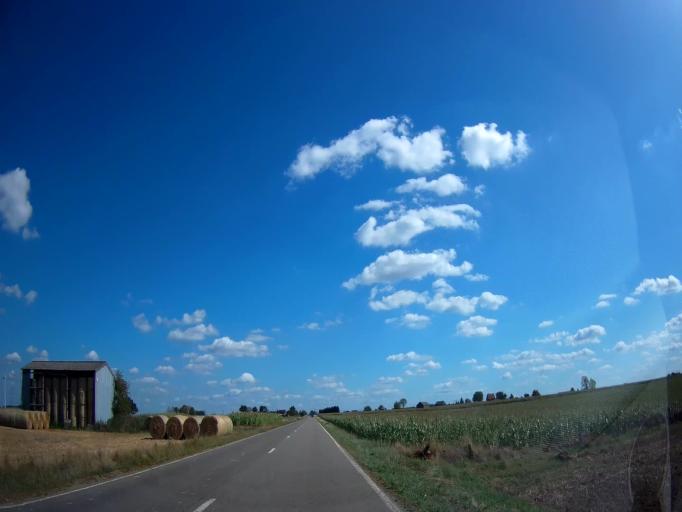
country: FR
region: Champagne-Ardenne
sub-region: Departement des Ardennes
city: Fromelennes
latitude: 50.1735
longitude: 4.8717
